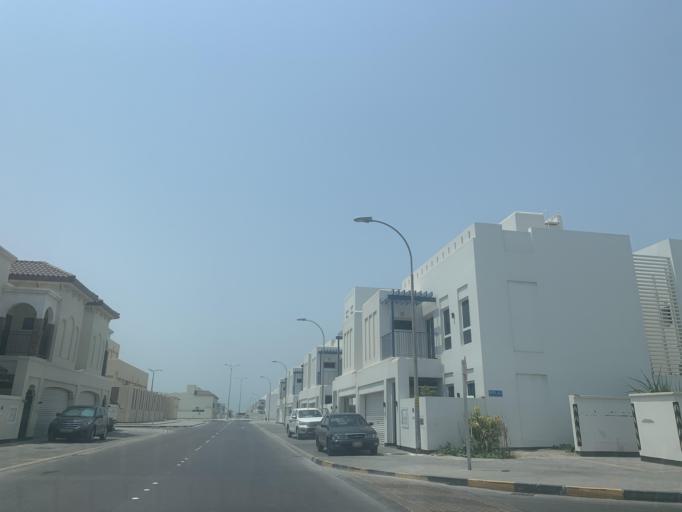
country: BH
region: Muharraq
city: Al Muharraq
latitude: 26.3115
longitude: 50.6254
